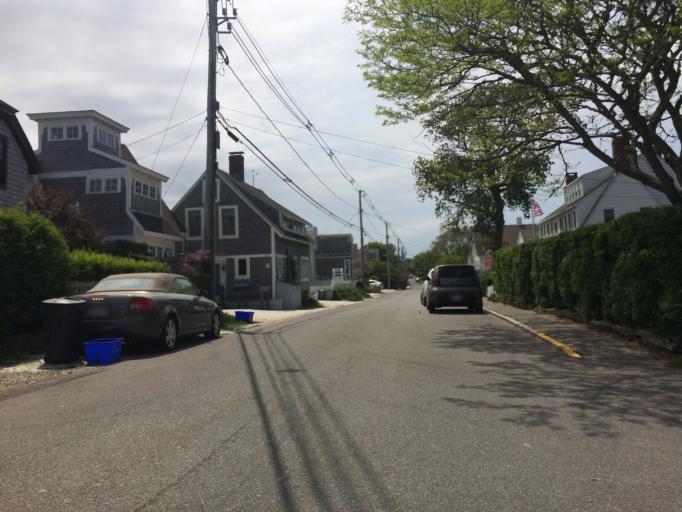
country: US
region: Massachusetts
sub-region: Barnstable County
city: Provincetown
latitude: 42.0605
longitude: -70.1678
